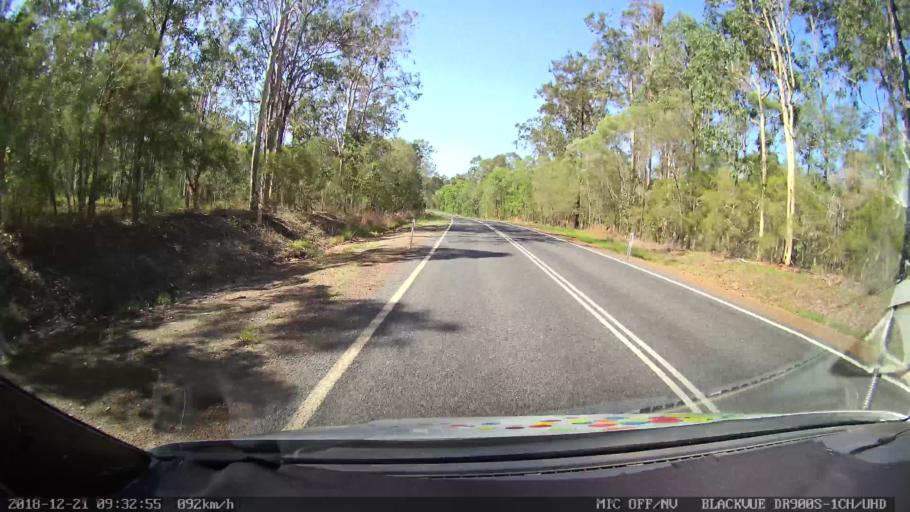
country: AU
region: New South Wales
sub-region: Clarence Valley
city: Grafton
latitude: -29.4769
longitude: 152.9764
